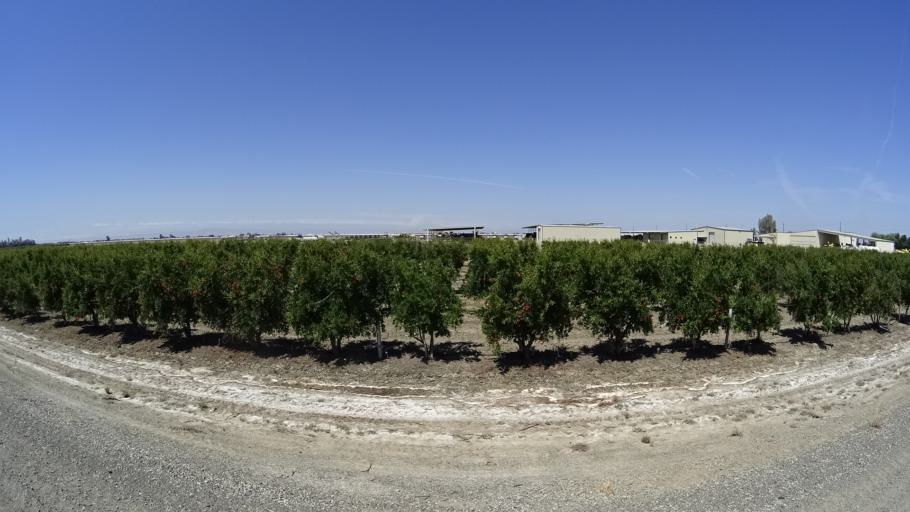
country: US
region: California
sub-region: Kings County
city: Stratford
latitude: 36.2237
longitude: -119.7982
